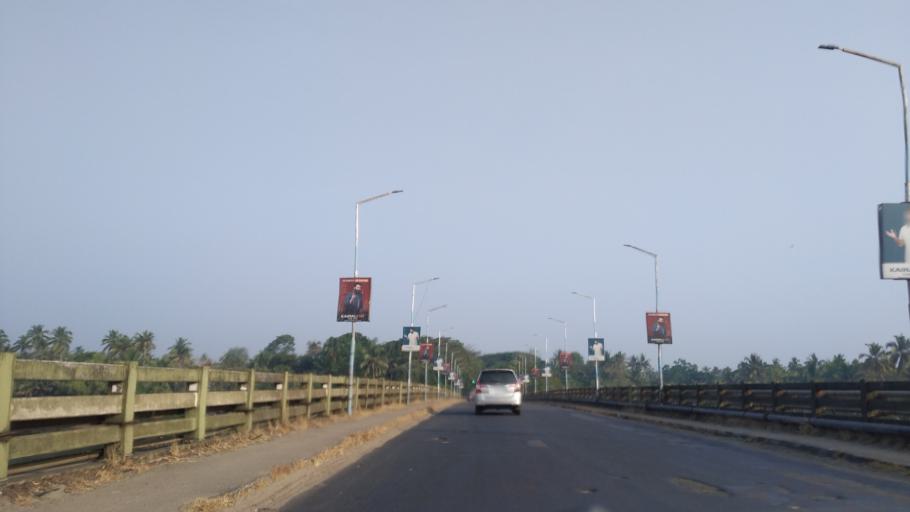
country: IN
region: Kerala
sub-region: Thrissur District
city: Kodungallur
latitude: 10.1991
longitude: 76.2006
